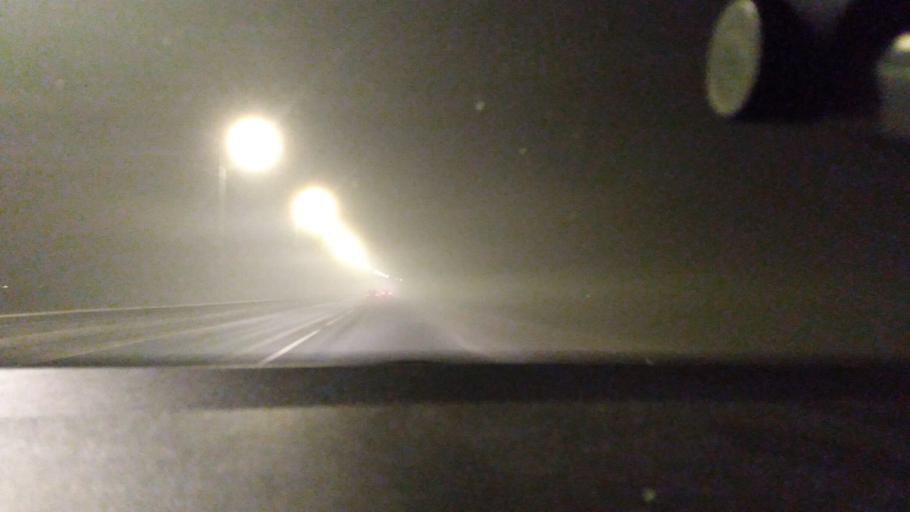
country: RU
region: Moskovskaya
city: Yegor'yevsk
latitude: 55.3941
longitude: 39.0701
